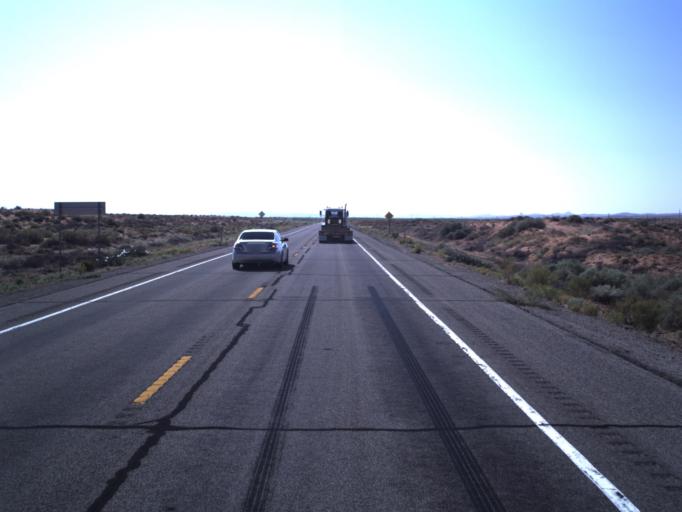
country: US
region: Utah
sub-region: San Juan County
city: Blanding
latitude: 37.2171
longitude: -109.6140
